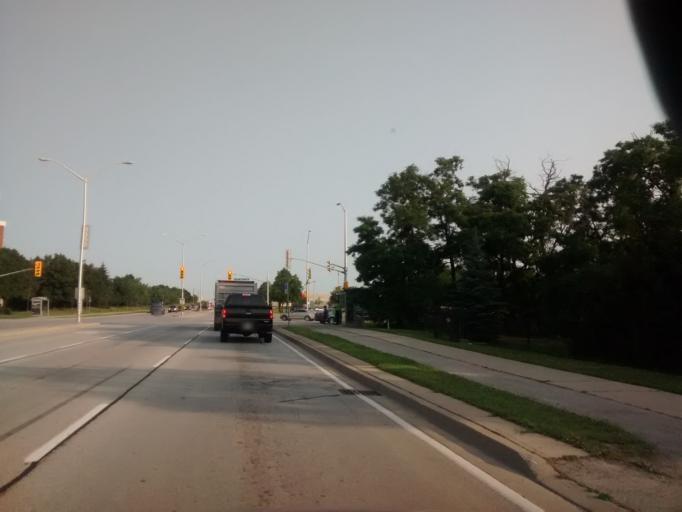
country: CA
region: Ontario
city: Oakville
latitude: 43.4341
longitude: -79.7381
